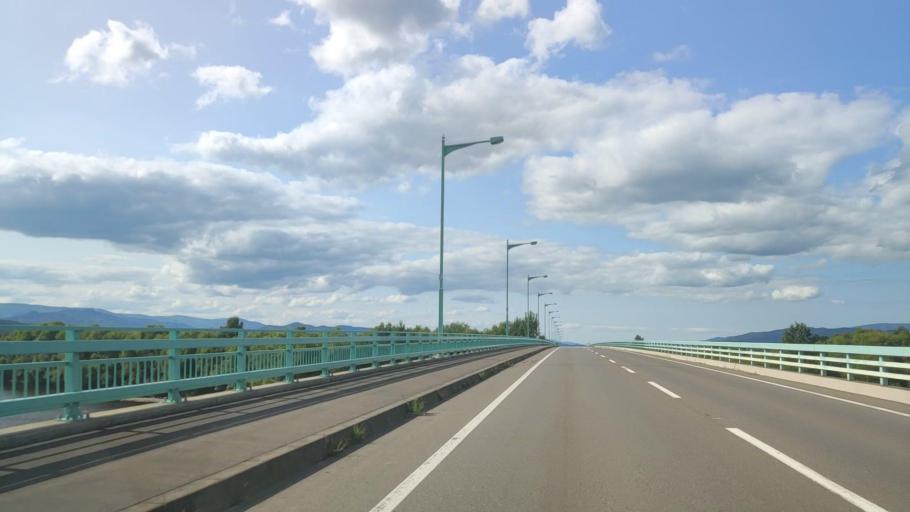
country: JP
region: Hokkaido
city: Nayoro
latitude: 44.4539
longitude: 142.3598
